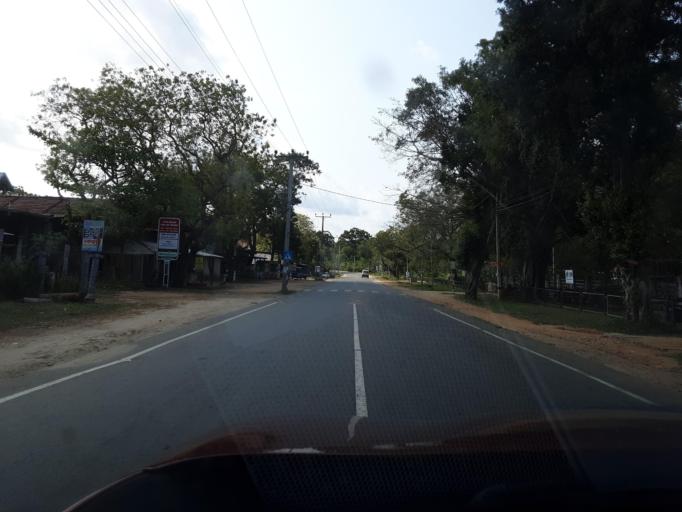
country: LK
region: Uva
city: Haputale
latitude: 6.3436
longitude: 81.2015
